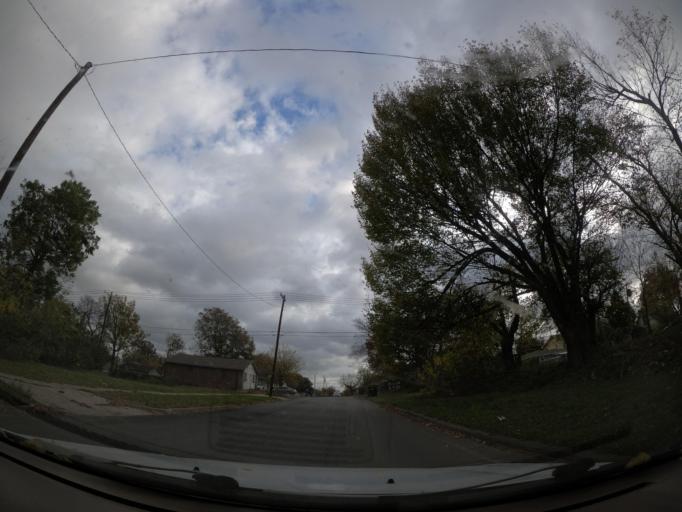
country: US
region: Oklahoma
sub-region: Tulsa County
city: Tulsa
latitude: 36.1638
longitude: -95.9618
